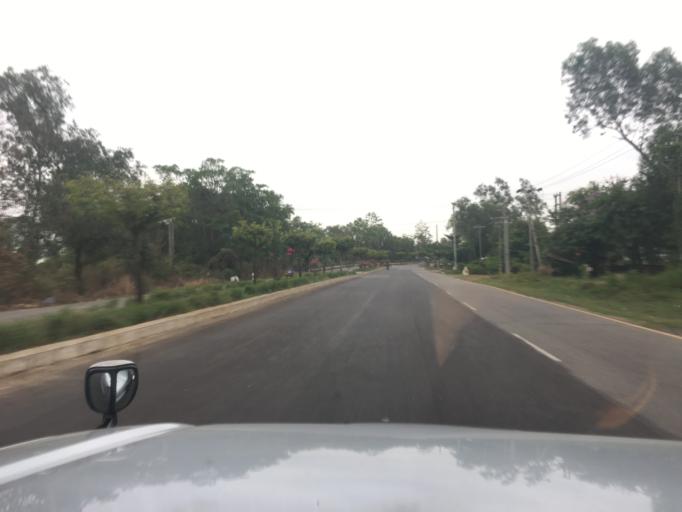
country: MM
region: Bago
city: Bago
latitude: 17.2198
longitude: 96.4355
